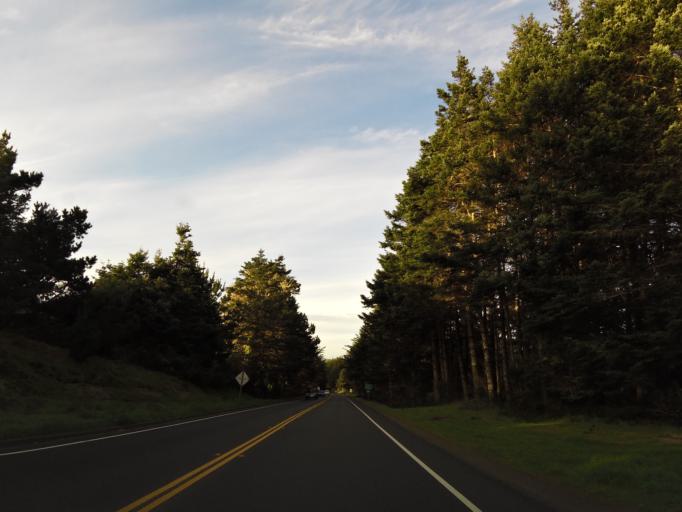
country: US
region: California
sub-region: Mendocino County
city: Fort Bragg
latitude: 39.3139
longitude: -123.7980
